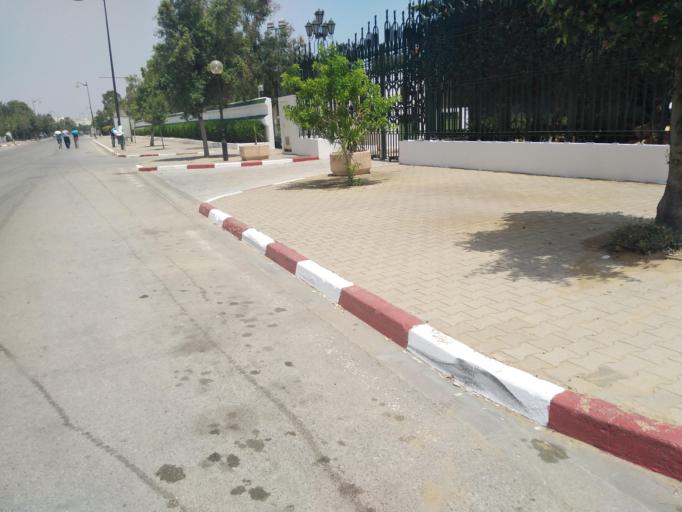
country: TN
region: Nabul
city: Al Hammamat
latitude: 36.3566
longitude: 10.5276
